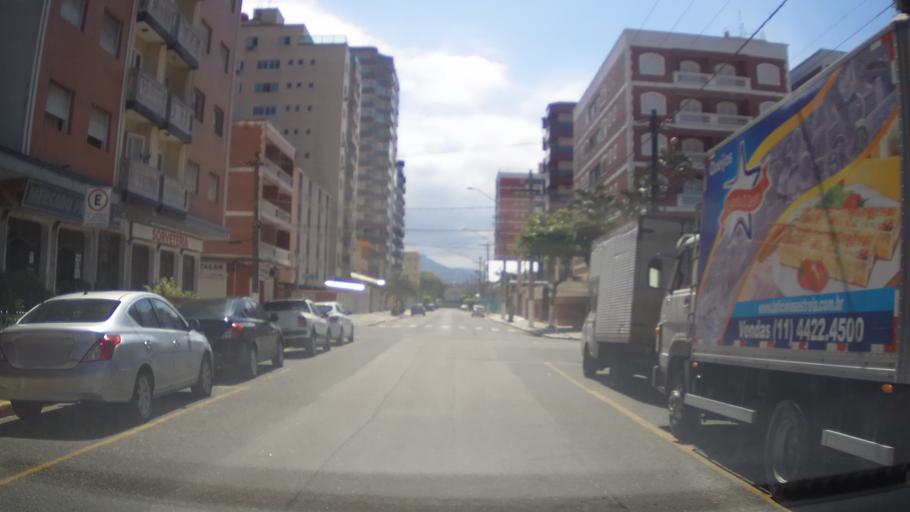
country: BR
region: Sao Paulo
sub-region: Praia Grande
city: Praia Grande
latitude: -24.0236
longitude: -46.4591
